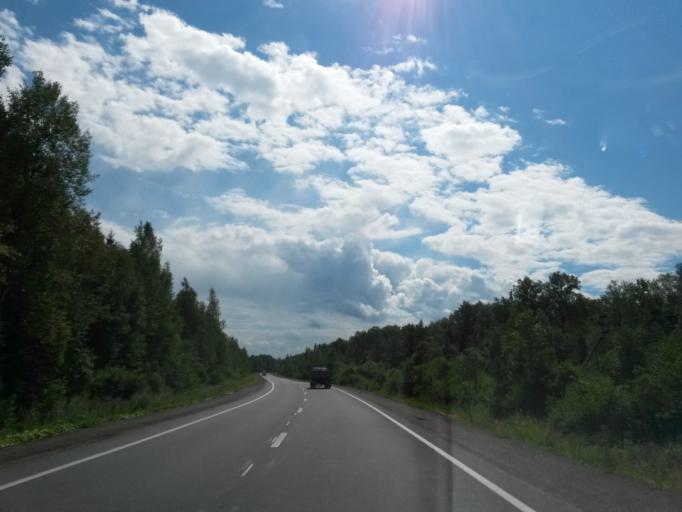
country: RU
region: Jaroslavl
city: Gavrilov-Yam
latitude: 57.2929
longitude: 39.9498
